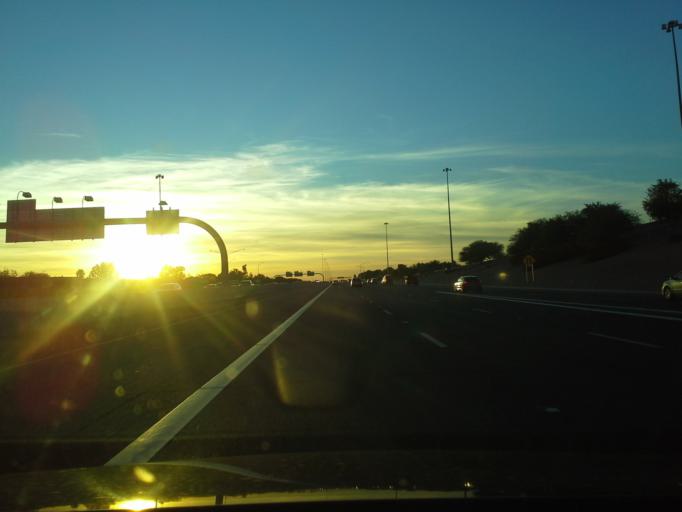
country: US
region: Arizona
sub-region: Pinal County
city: Apache Junction
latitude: 33.3868
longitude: -111.6529
